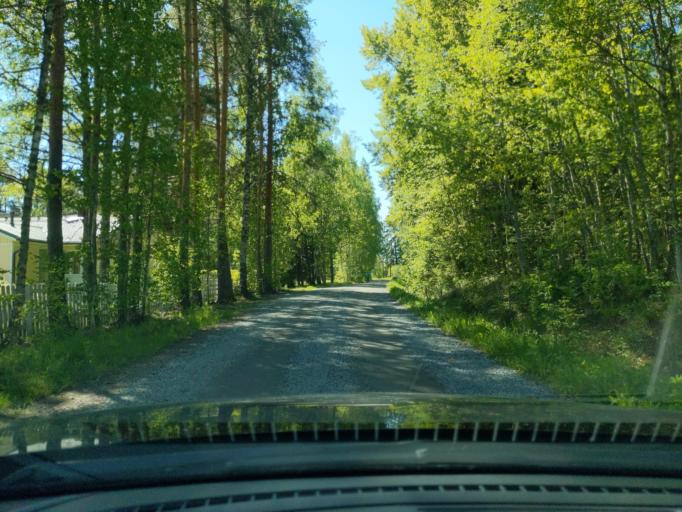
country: FI
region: Paijanne Tavastia
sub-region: Lahti
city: Lahti
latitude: 61.0614
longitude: 25.6665
